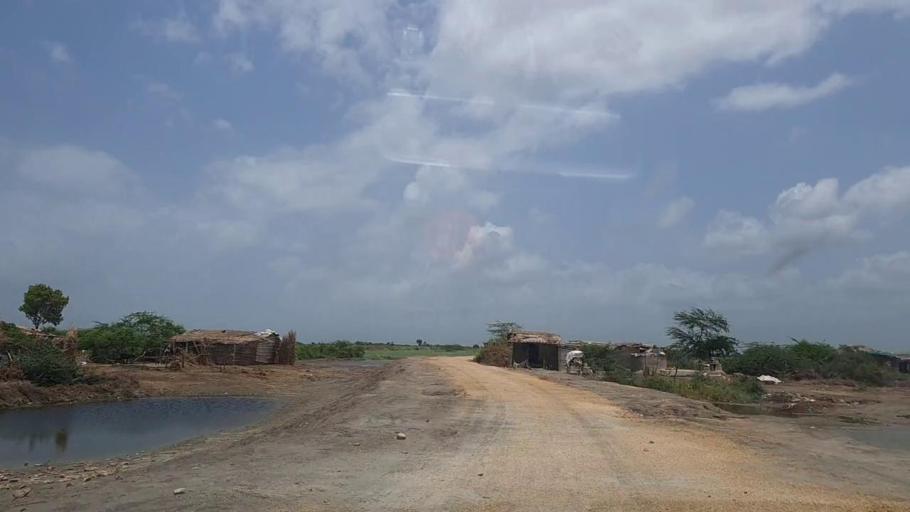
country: PK
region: Sindh
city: Thatta
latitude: 24.6213
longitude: 68.0343
